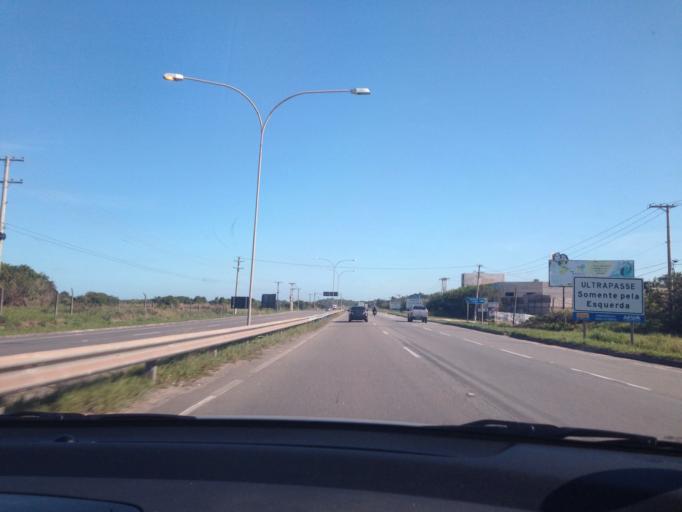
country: BR
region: Espirito Santo
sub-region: Vila Velha
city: Vila Velha
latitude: -20.4522
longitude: -40.3361
